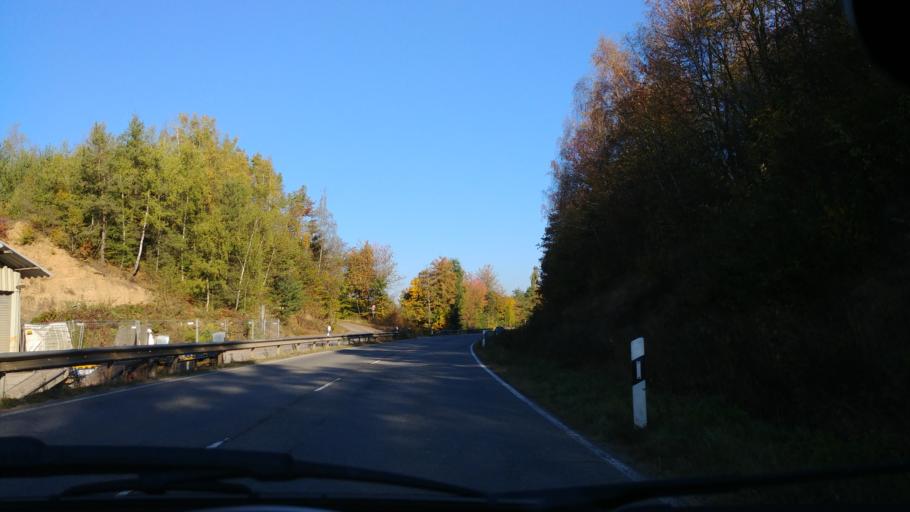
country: DE
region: Rheinland-Pfalz
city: Oelsberg
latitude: 50.2069
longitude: 7.8386
